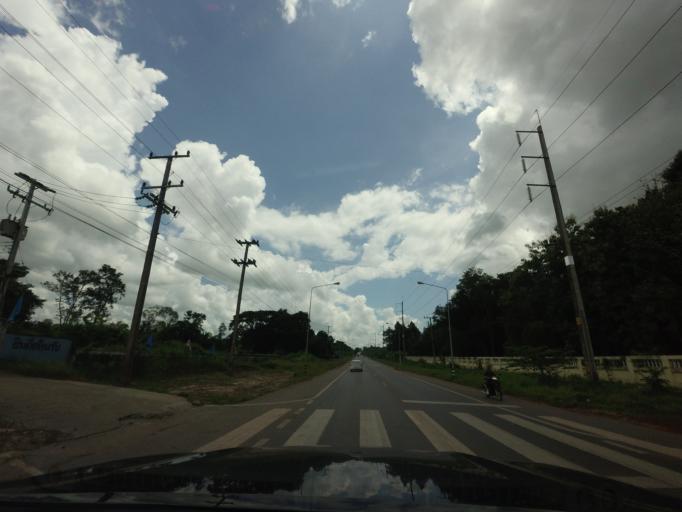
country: TH
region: Nong Khai
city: Sa Khrai
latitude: 17.5877
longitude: 102.6115
